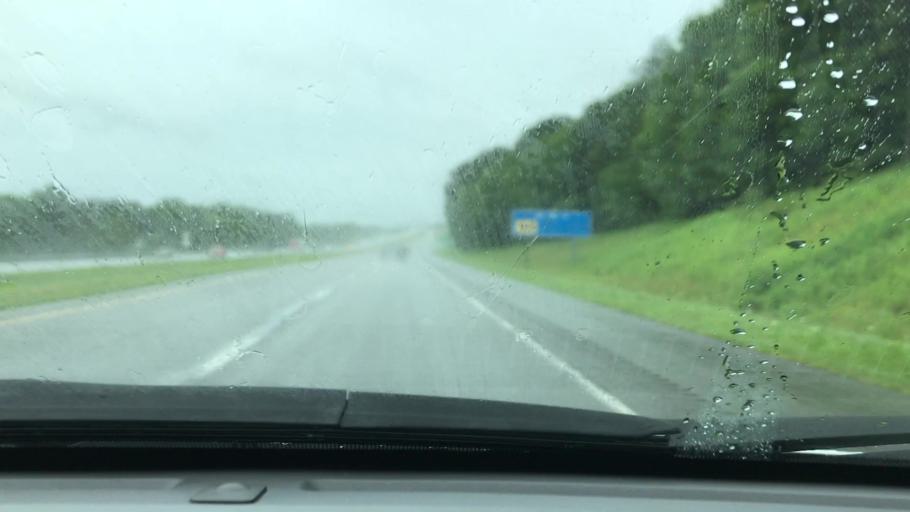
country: US
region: Pennsylvania
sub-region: Blair County
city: Tyrone
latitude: 40.7042
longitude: -78.2032
